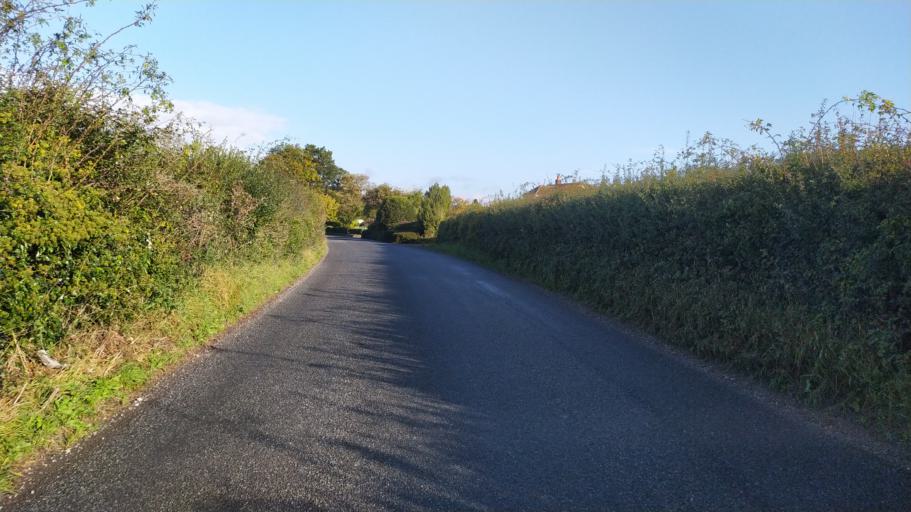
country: GB
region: England
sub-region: Wiltshire
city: Ansty
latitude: 50.9287
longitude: -2.0606
